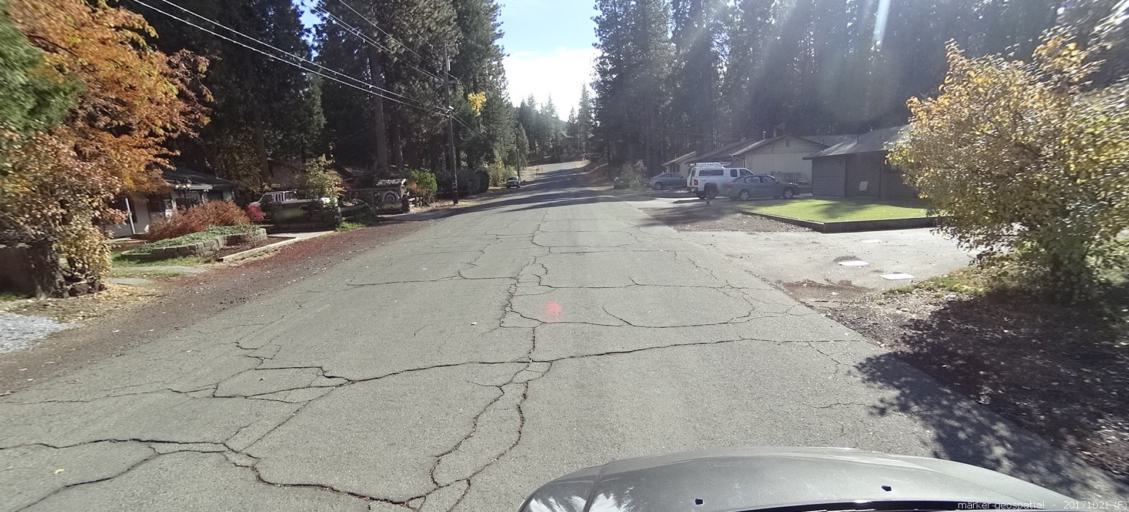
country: US
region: California
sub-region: Shasta County
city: Burney
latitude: 40.8760
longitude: -121.6575
